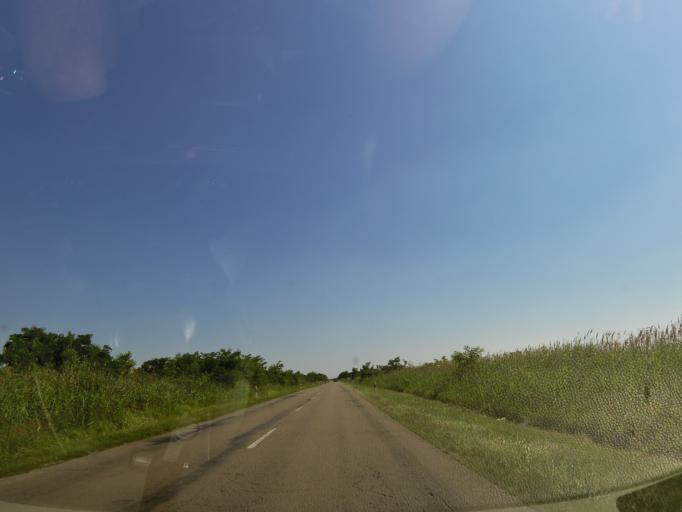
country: HU
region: Jasz-Nagykun-Szolnok
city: Fegyvernek
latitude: 47.2504
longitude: 20.5542
